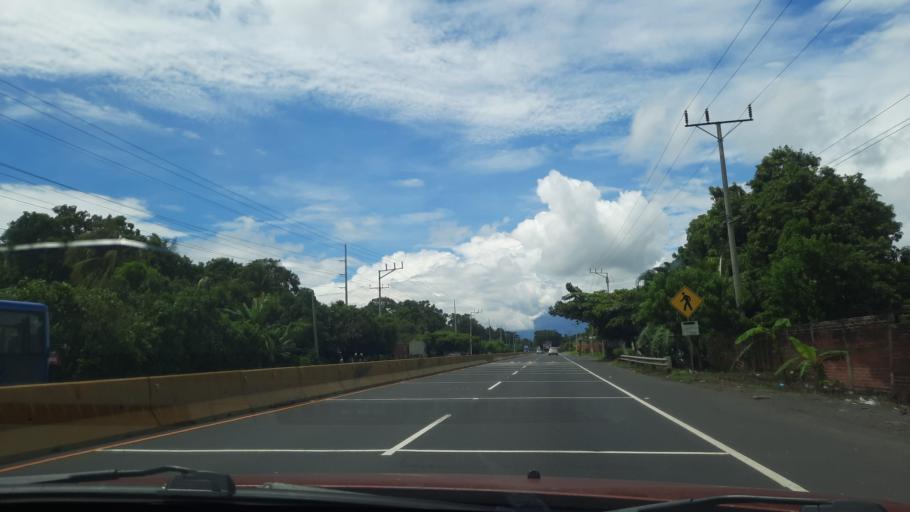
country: SV
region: Sonsonate
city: Acajutla
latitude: 13.6422
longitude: -89.7742
